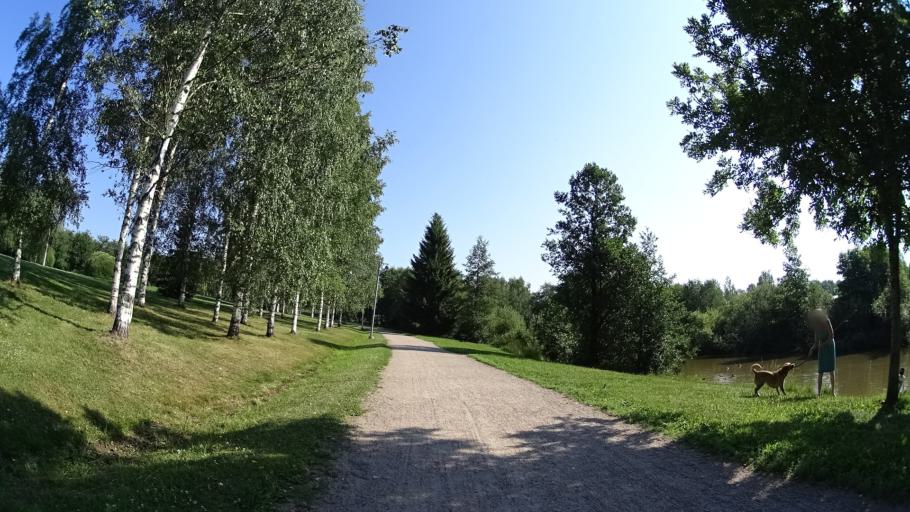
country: FI
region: Uusimaa
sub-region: Helsinki
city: Vantaa
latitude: 60.3203
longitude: 25.0851
